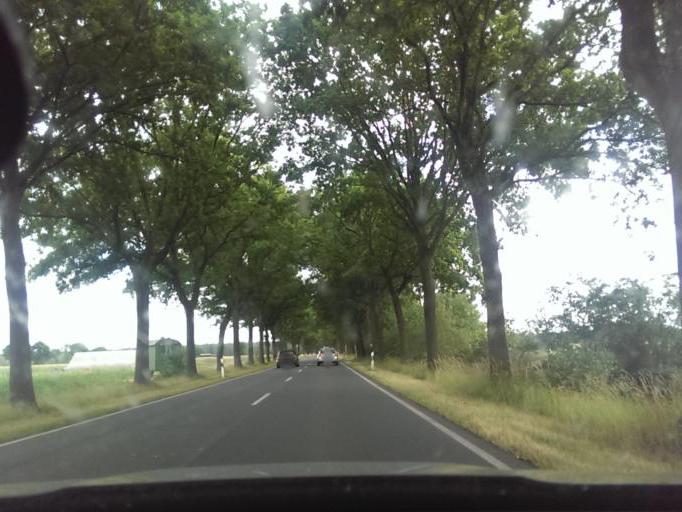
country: DE
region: Lower Saxony
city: Essel
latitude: 52.6638
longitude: 9.6641
